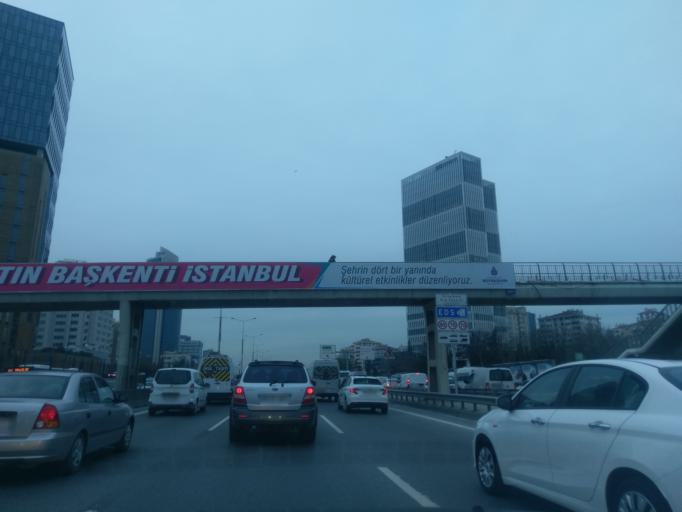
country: TR
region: Istanbul
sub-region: Atasehir
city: Atasehir
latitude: 40.9704
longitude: 29.1019
